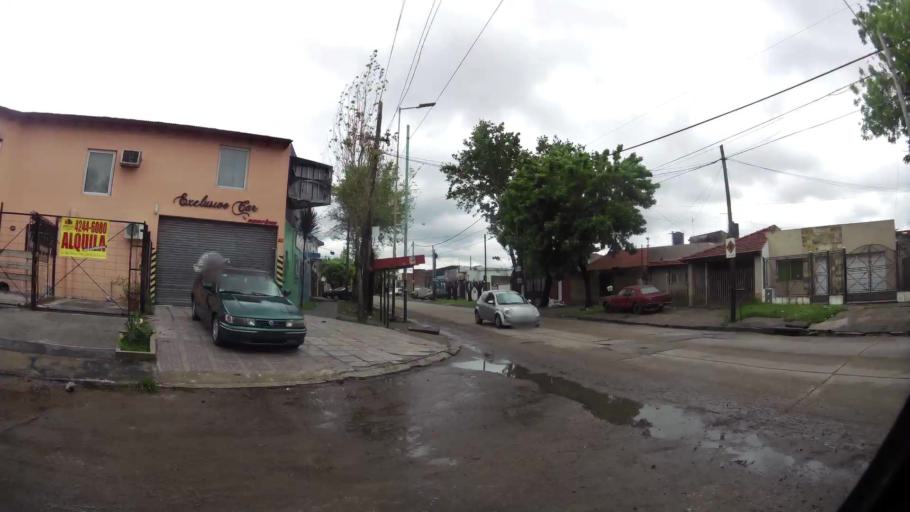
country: AR
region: Buenos Aires
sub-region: Partido de Lomas de Zamora
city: Lomas de Zamora
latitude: -34.7497
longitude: -58.3706
